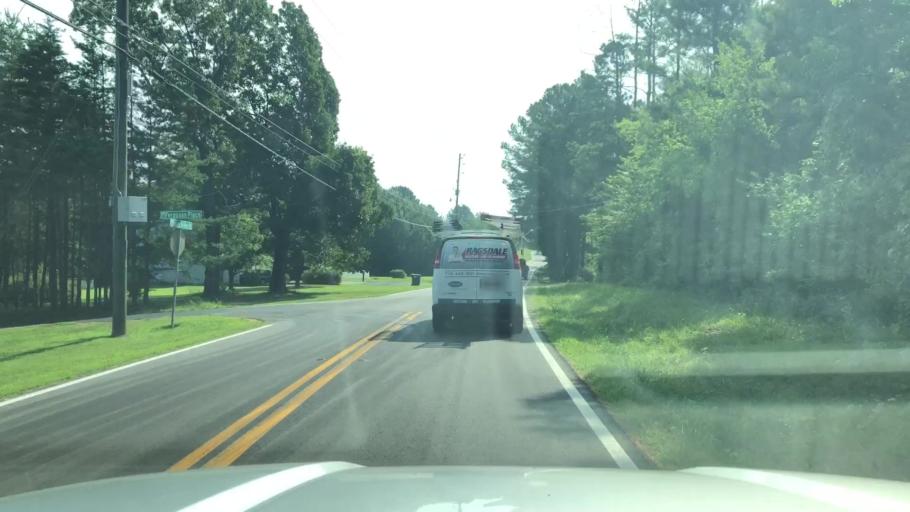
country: US
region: Georgia
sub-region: Bartow County
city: Emerson
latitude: 34.0516
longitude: -84.8288
